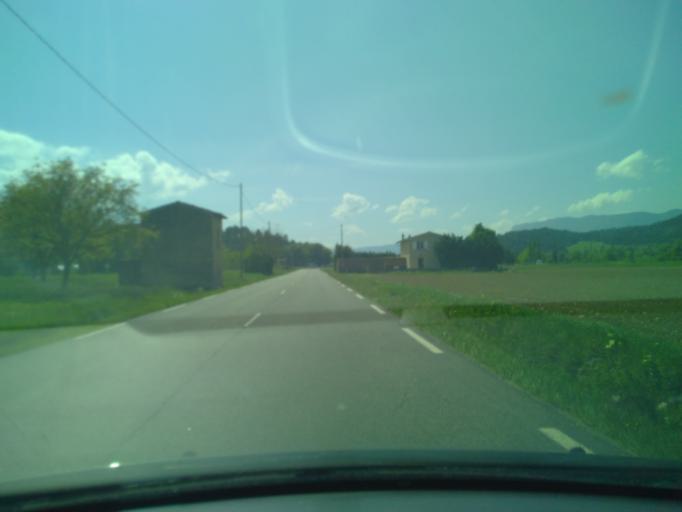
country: FR
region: Rhone-Alpes
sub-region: Departement de la Drome
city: Die
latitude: 44.7330
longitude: 5.3905
